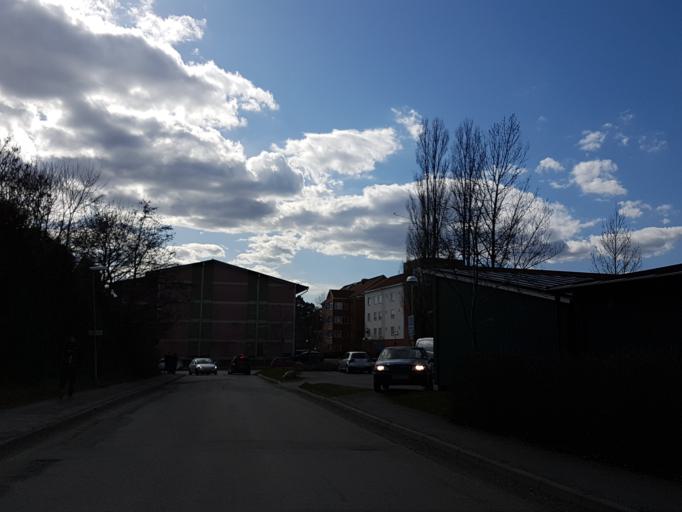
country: SE
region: Stockholm
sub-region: Nacka Kommun
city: Alta
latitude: 59.2656
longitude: 18.1436
